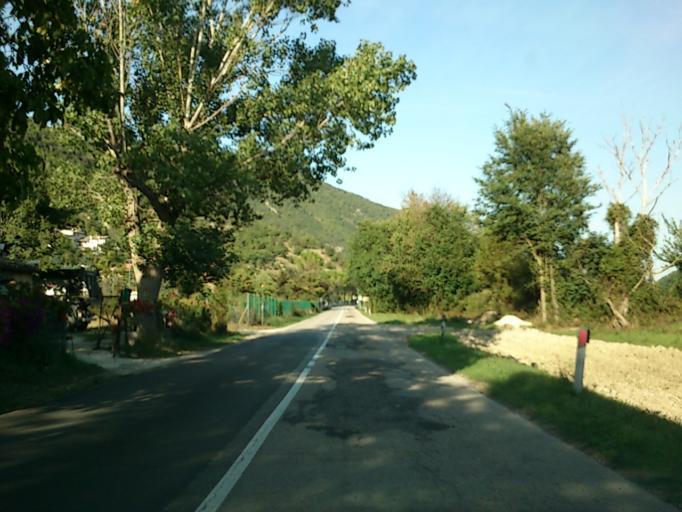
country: IT
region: The Marches
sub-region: Provincia di Pesaro e Urbino
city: Fossombrone
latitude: 43.6814
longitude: 12.7673
